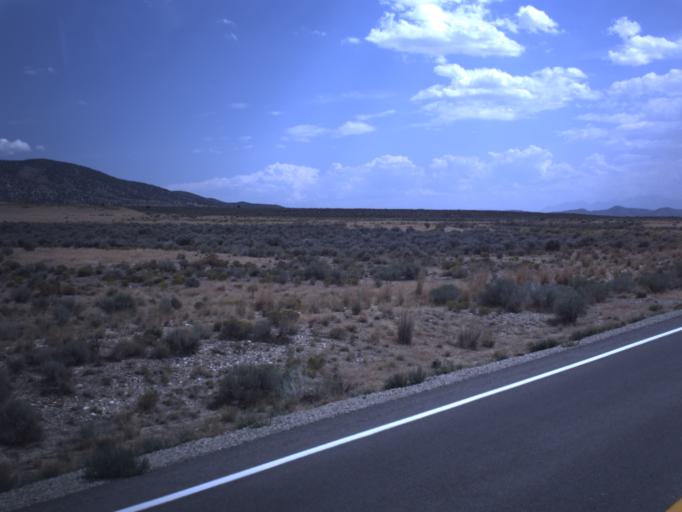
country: US
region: Utah
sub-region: Tooele County
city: Tooele
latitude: 40.3006
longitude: -112.2764
